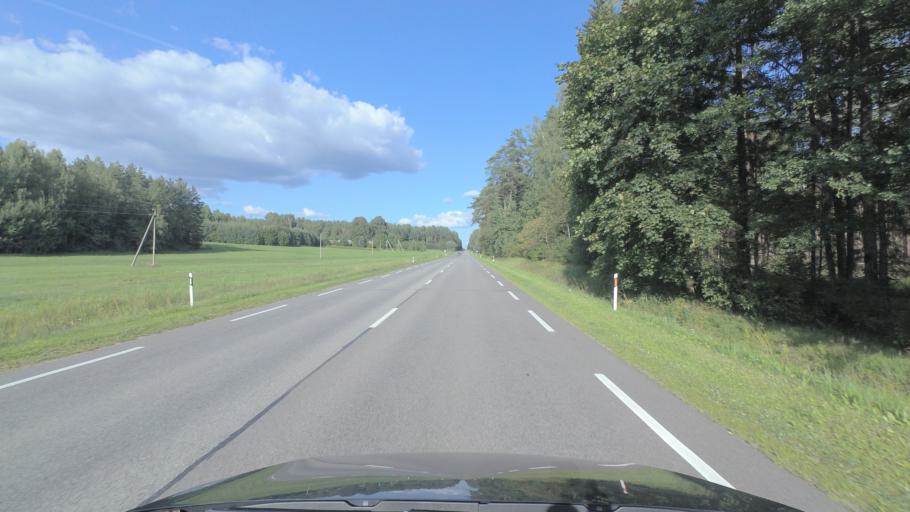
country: LT
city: Pabrade
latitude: 54.9624
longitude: 25.7011
